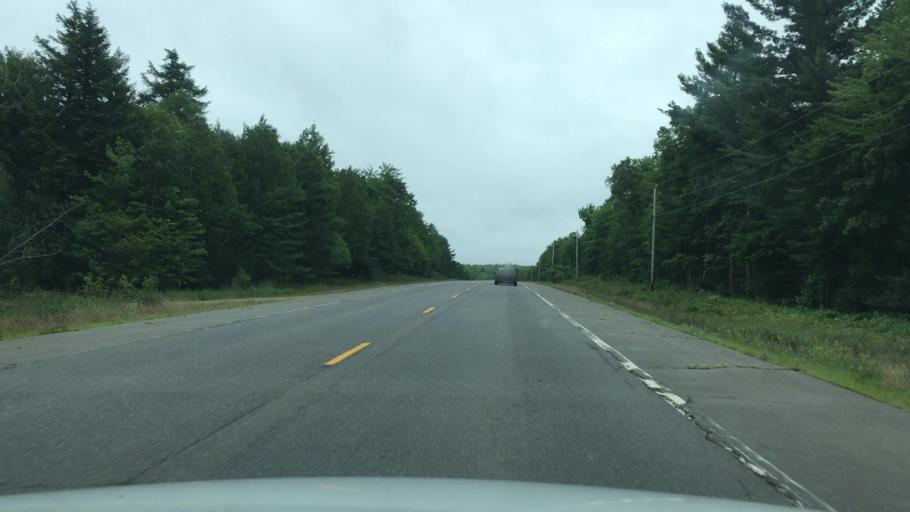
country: US
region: Maine
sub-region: Hancock County
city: Franklin
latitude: 44.8351
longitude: -68.1404
